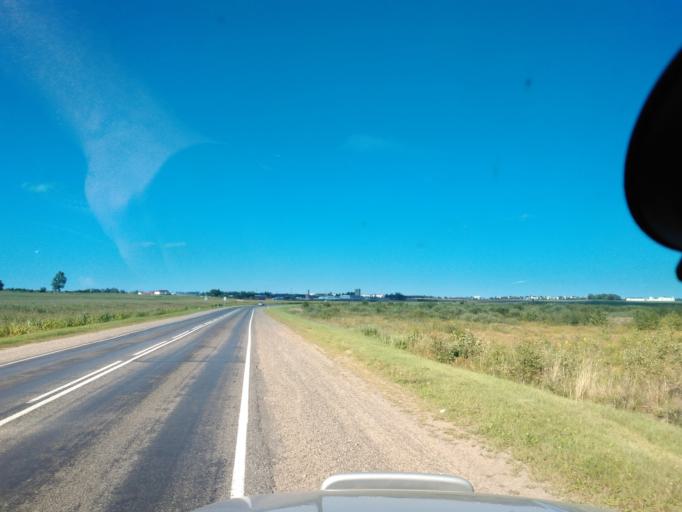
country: BY
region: Minsk
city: Dzyarzhynsk
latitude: 53.6650
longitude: 27.0880
